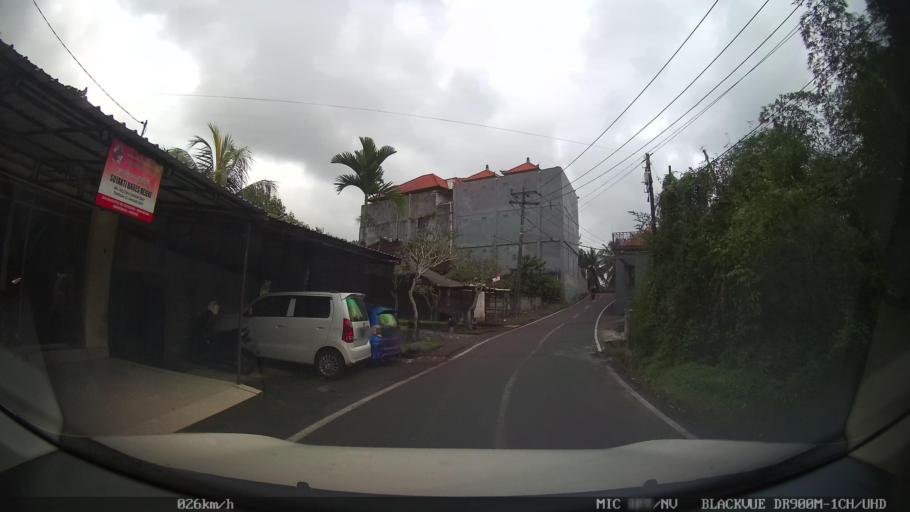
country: ID
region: Bali
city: Banjar Mambalkajanan
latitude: -8.5597
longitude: 115.2179
